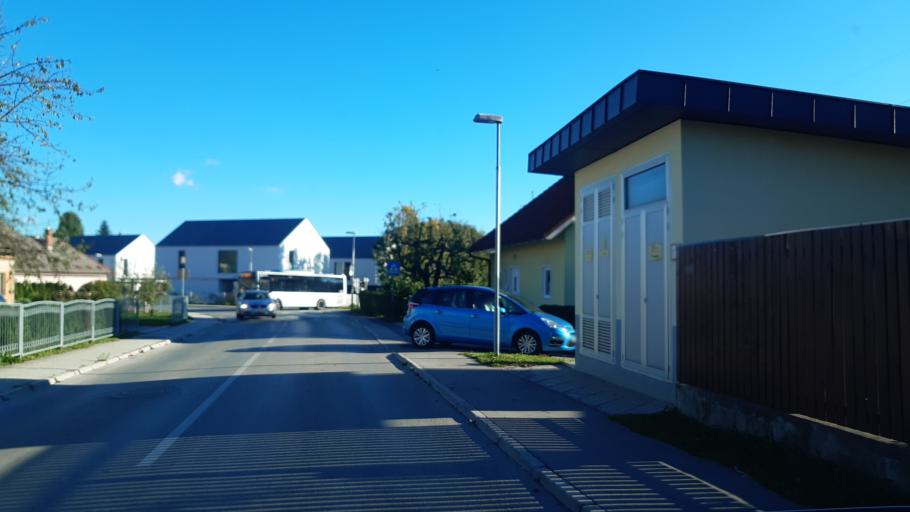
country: SI
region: Kranj
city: Zgornje Bitnje
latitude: 46.2296
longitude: 14.3371
